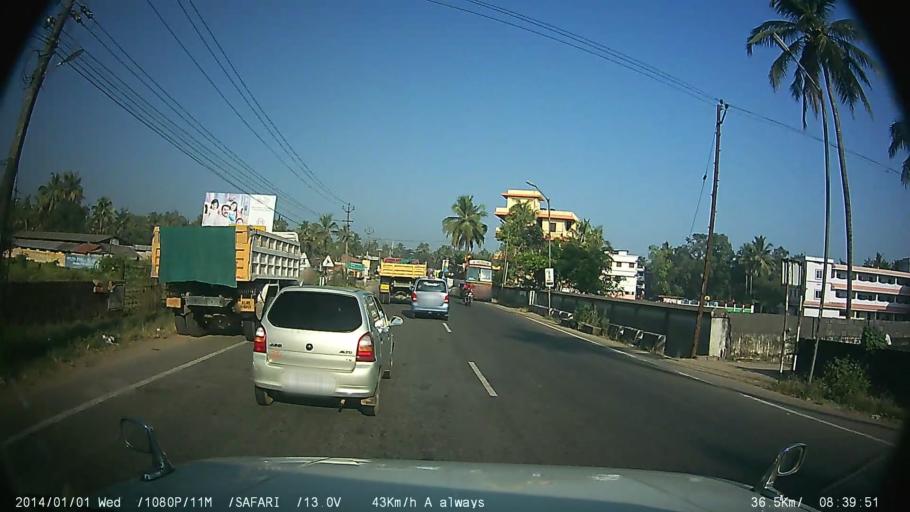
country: IN
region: Kerala
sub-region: Ernakulam
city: Perumpavur
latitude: 10.1576
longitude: 76.4448
